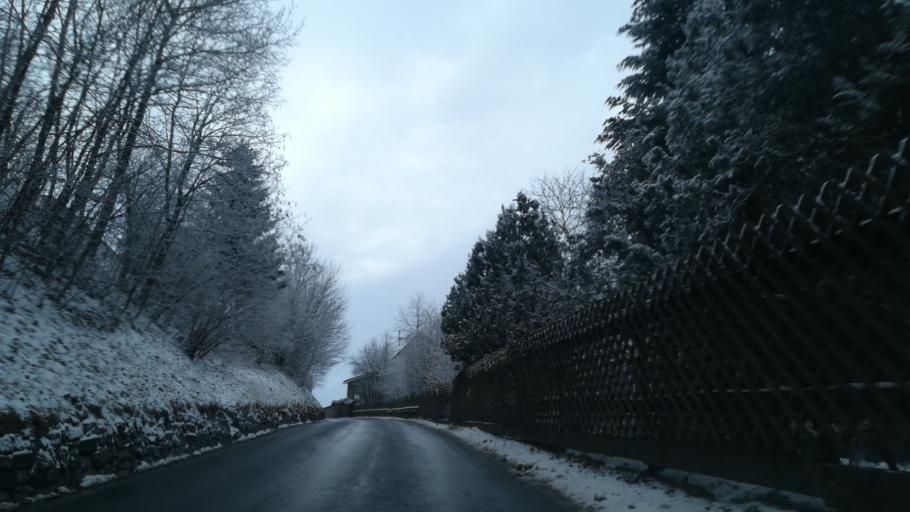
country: AT
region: Styria
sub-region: Politischer Bezirk Murtal
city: Poels
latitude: 47.2090
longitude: 14.6284
